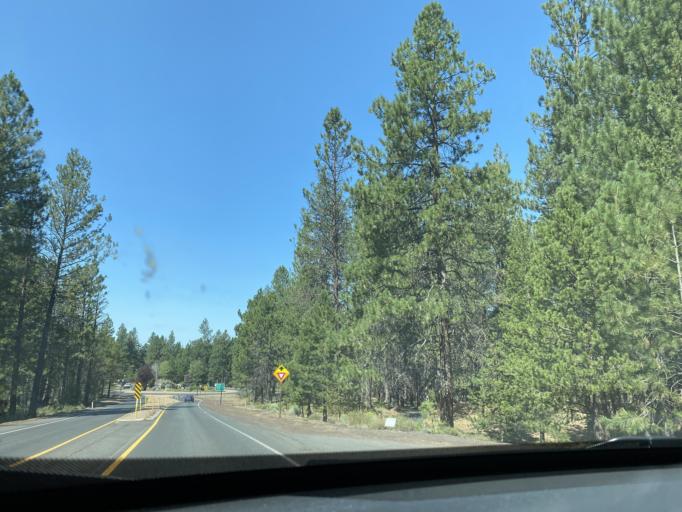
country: US
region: Oregon
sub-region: Deschutes County
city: Sunriver
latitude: 43.8694
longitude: -121.4310
